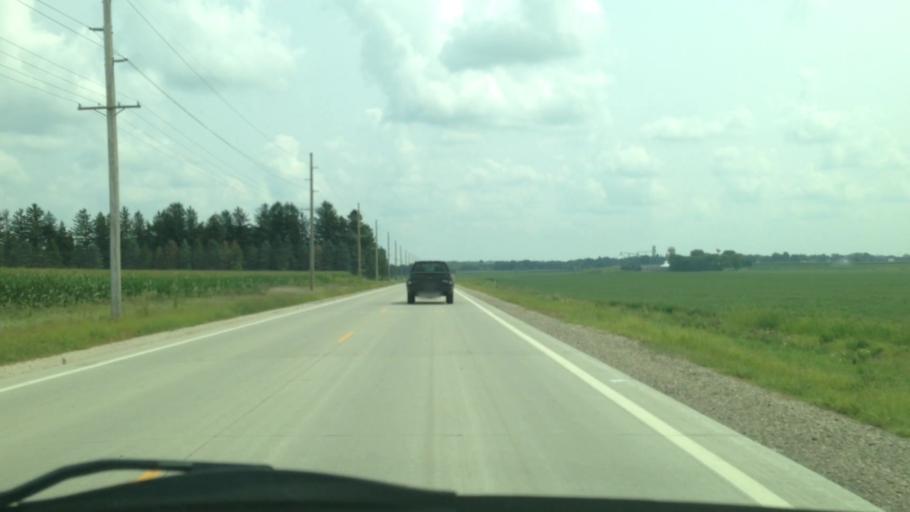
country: US
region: Minnesota
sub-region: Wabasha County
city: Elgin
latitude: 44.1366
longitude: -92.2855
